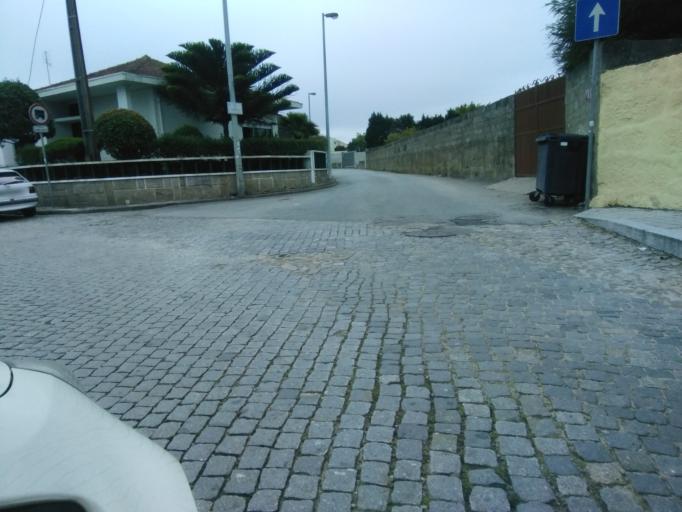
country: PT
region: Porto
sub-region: Matosinhos
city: Santa Cruz do Bispo
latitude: 41.2246
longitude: -8.7033
